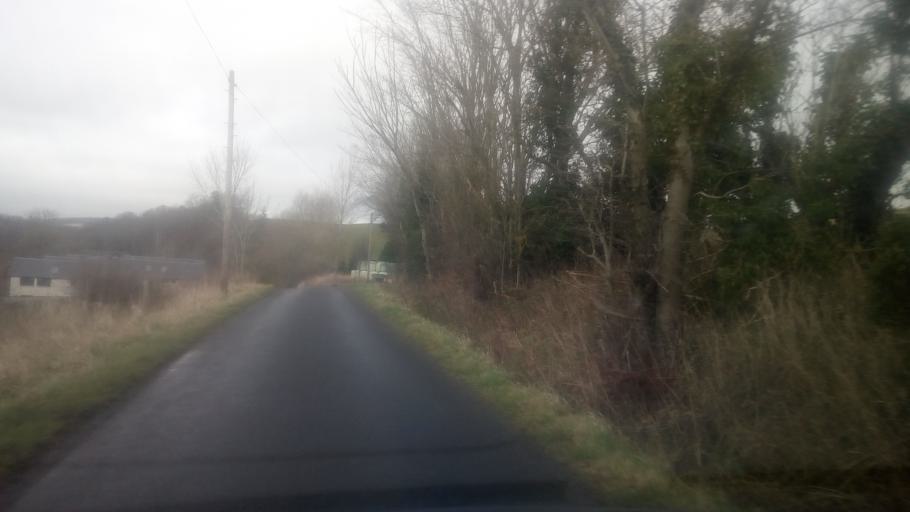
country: GB
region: Scotland
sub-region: The Scottish Borders
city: Jedburgh
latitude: 55.4886
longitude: -2.5412
